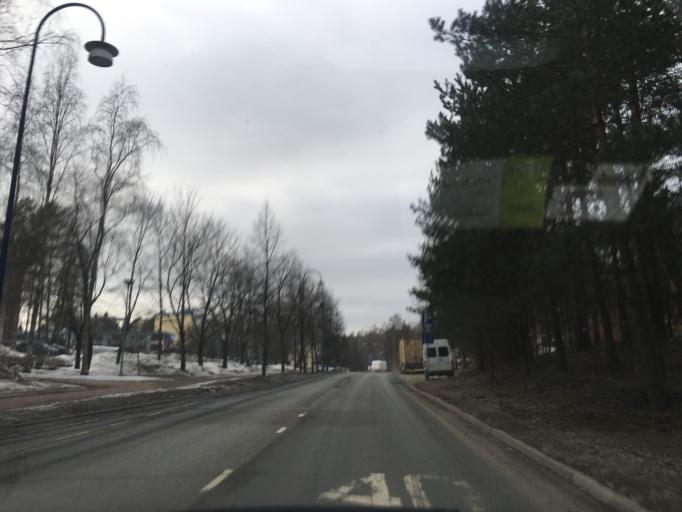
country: FI
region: Uusimaa
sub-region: Helsinki
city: Vantaa
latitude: 60.3232
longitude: 25.0788
